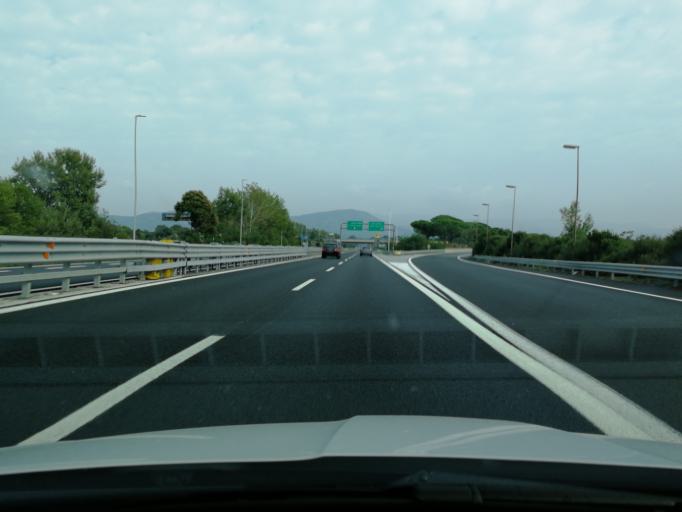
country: IT
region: Latium
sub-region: Citta metropolitana di Roma Capitale
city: Corcolle
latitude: 41.9272
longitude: 12.7344
